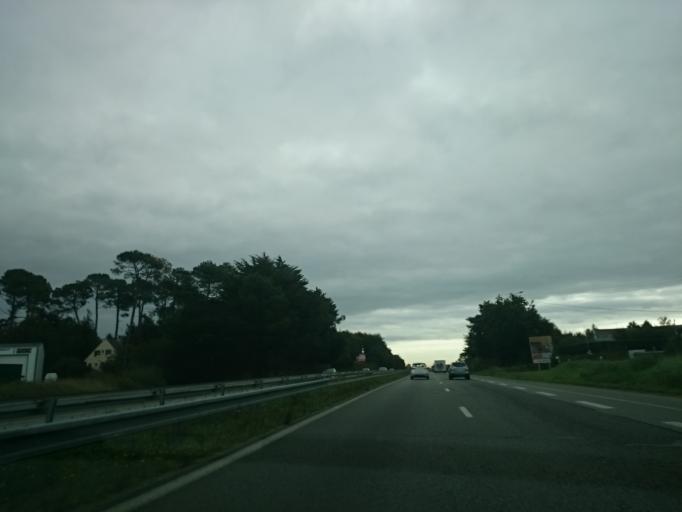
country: FR
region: Brittany
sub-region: Departement du Morbihan
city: Ploeren
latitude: 47.6608
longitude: -2.8545
